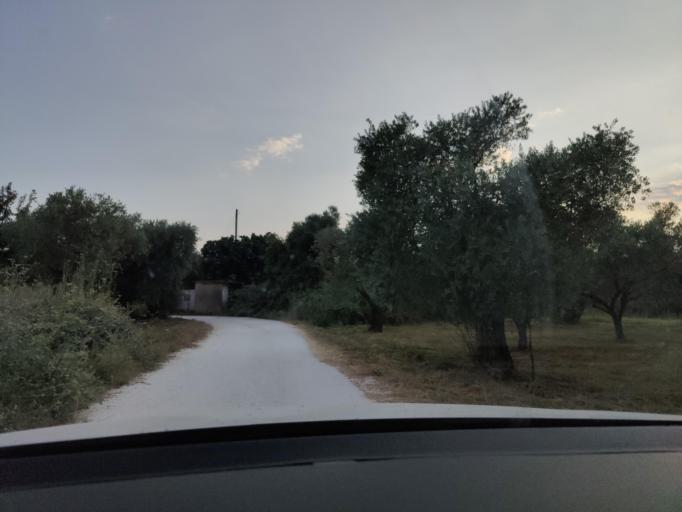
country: GR
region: East Macedonia and Thrace
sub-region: Nomos Kavalas
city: Prinos
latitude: 40.7492
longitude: 24.5742
